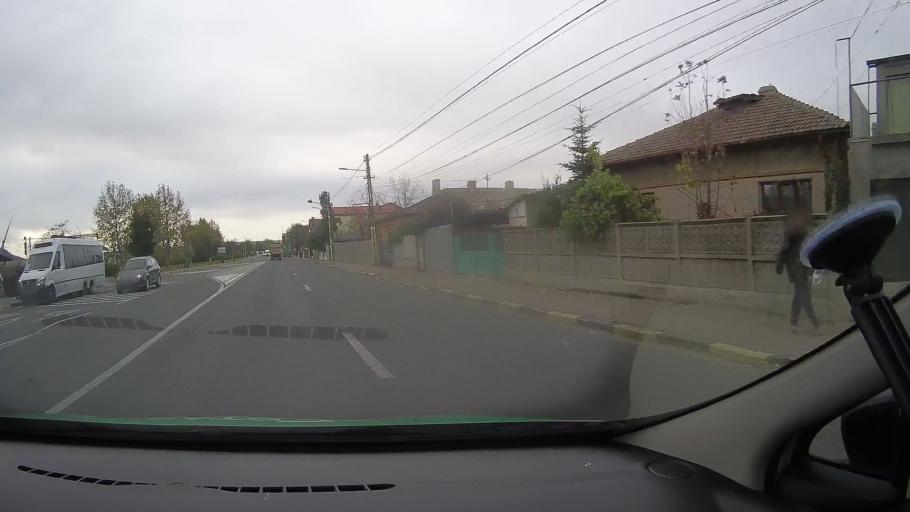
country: RO
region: Constanta
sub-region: Oras Murfatlar
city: Murfatlar
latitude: 44.1723
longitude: 28.4174
